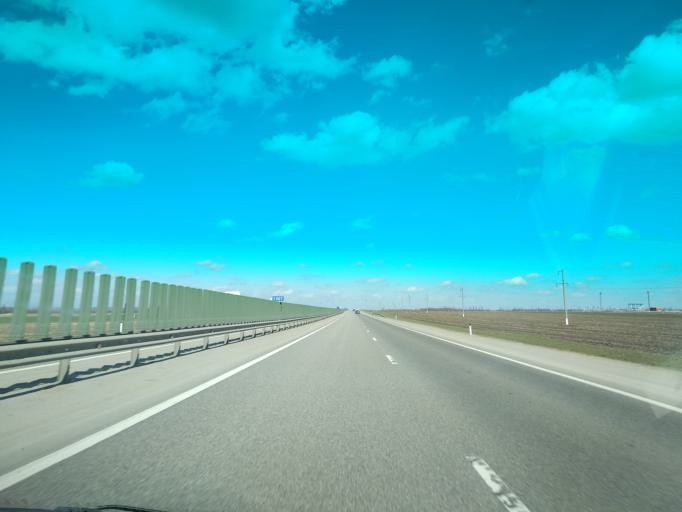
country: RU
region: Krasnodarskiy
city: Dinskaya
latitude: 45.2647
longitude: 39.2077
